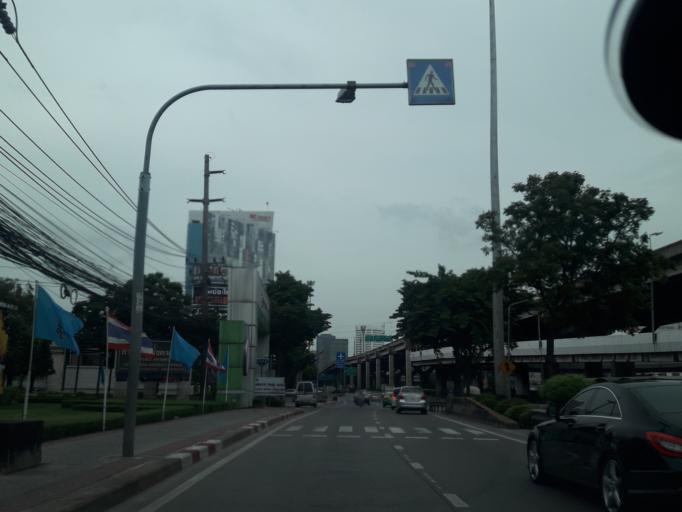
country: TH
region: Bangkok
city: Chatuchak
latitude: 13.8286
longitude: 100.5584
